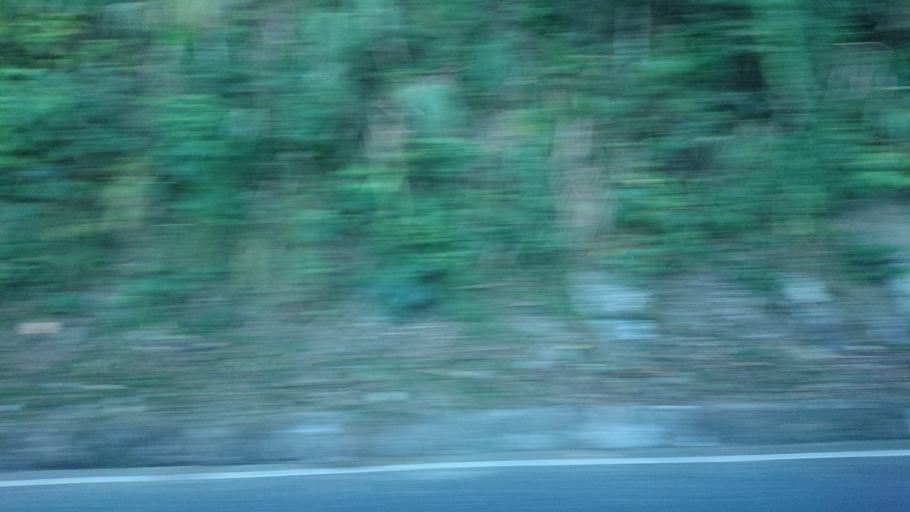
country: TW
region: Taiwan
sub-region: Chiayi
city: Jiayi Shi
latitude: 23.4646
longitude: 120.7186
